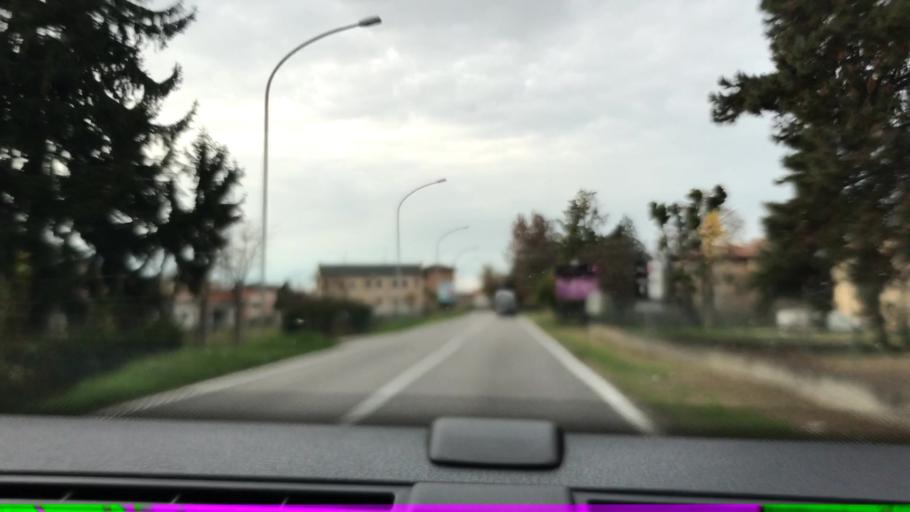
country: IT
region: Lombardy
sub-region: Provincia di Mantova
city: San Benedetto Po
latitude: 45.0372
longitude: 10.9304
